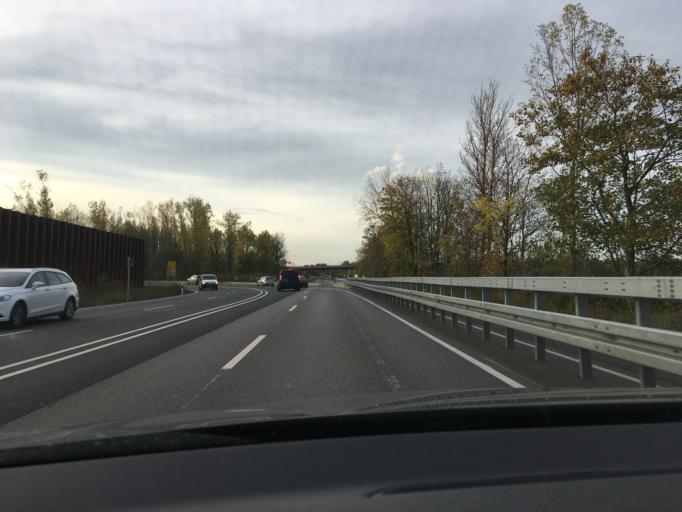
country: DE
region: Saxony
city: Bohlen
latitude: 51.2180
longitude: 12.3856
